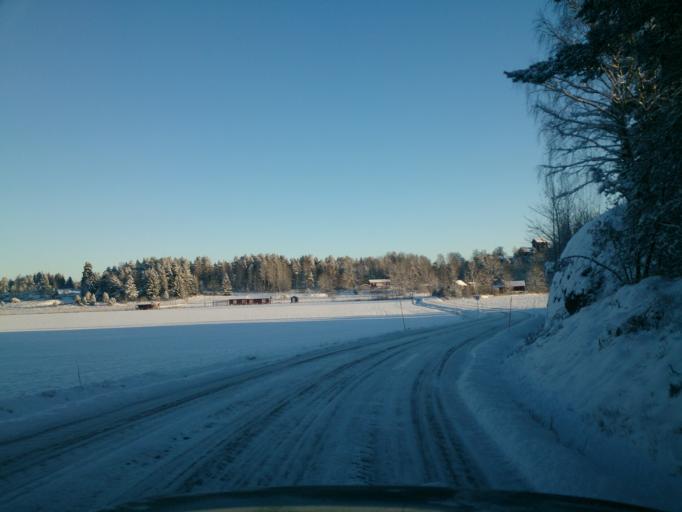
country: SE
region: OEstergoetland
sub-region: Norrkopings Kommun
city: Krokek
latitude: 58.5057
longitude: 16.5836
